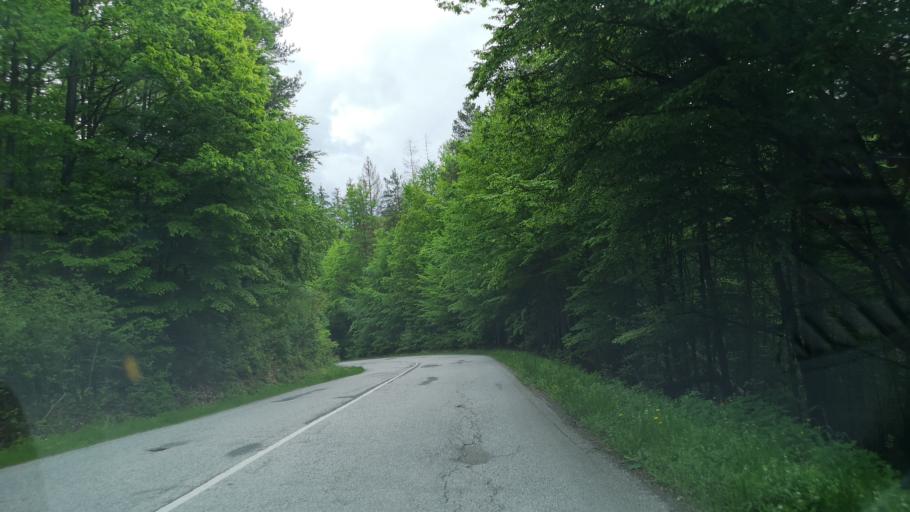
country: SK
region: Kosicky
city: Dobsina
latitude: 48.7151
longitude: 20.4078
